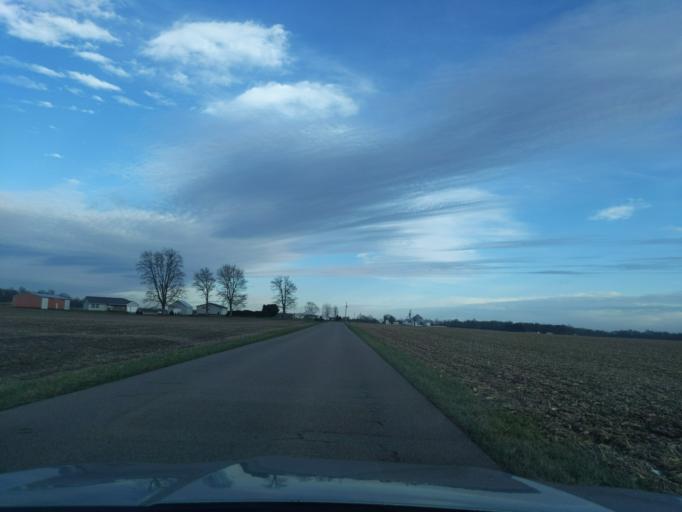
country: US
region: Indiana
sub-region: Decatur County
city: Westport
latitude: 39.2347
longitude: -85.5590
